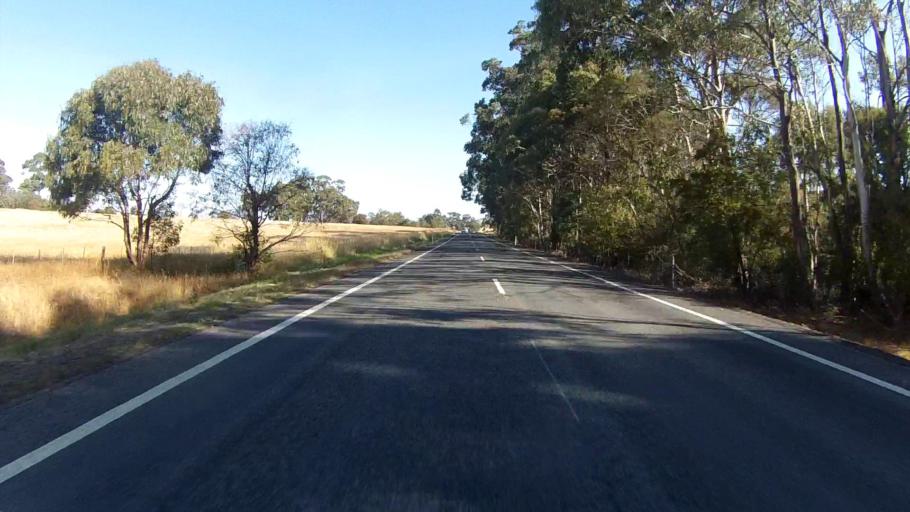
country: AU
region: Tasmania
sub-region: Sorell
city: Sorell
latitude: -42.6961
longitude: 147.5259
